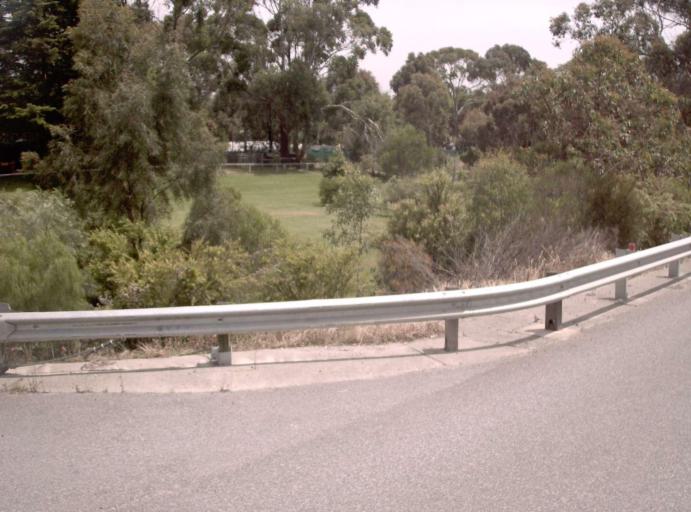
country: AU
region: Victoria
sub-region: Casey
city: Cranbourne South
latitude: -38.1410
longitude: 145.2269
